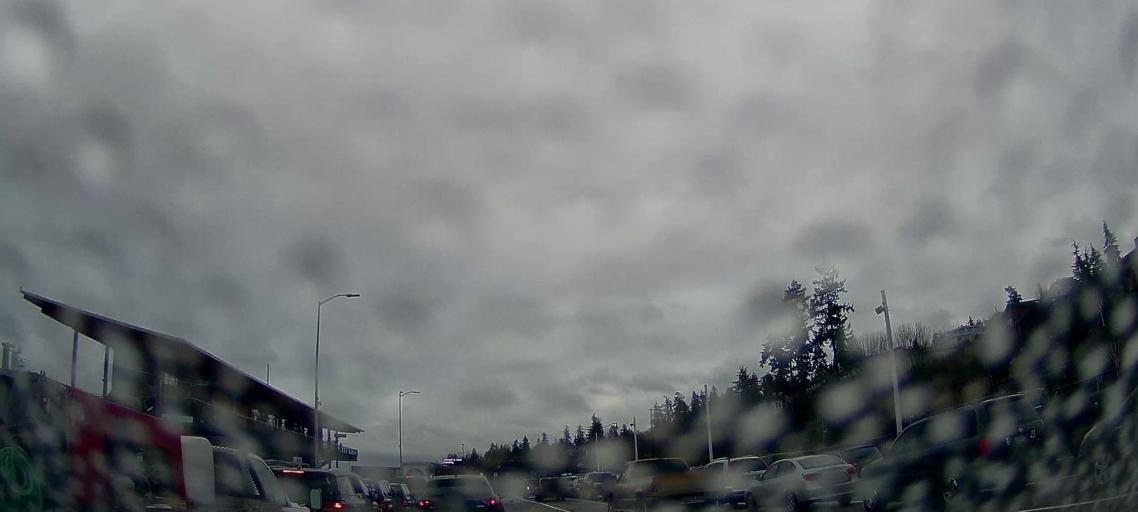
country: US
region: Washington
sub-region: Snohomish County
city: Mukilteo
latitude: 47.9497
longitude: -122.2980
